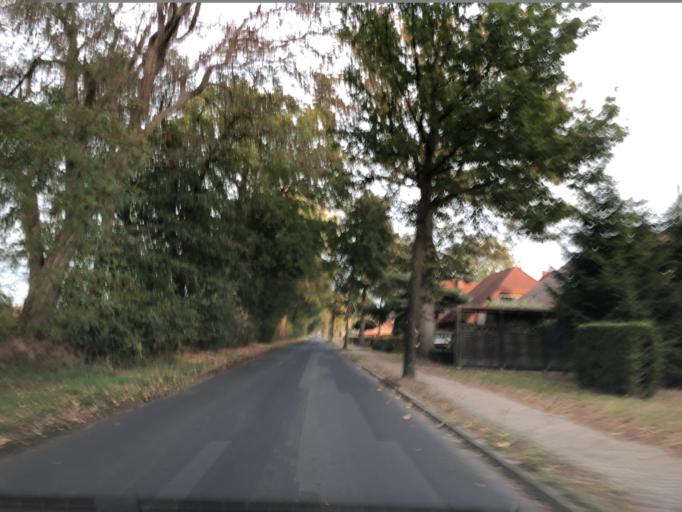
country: DE
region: Lower Saxony
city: Lehe
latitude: 53.0262
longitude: 7.3312
